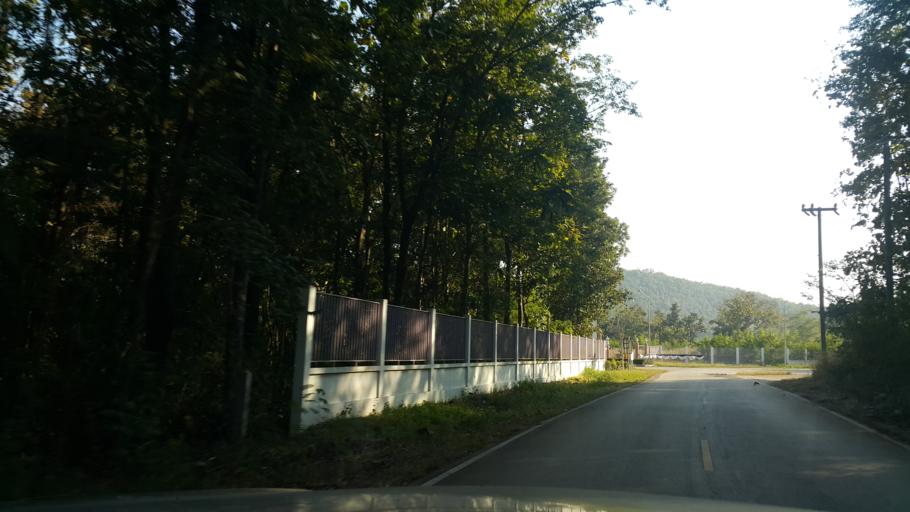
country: TH
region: Lamphun
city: Mae Tha
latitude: 18.5126
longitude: 99.1105
